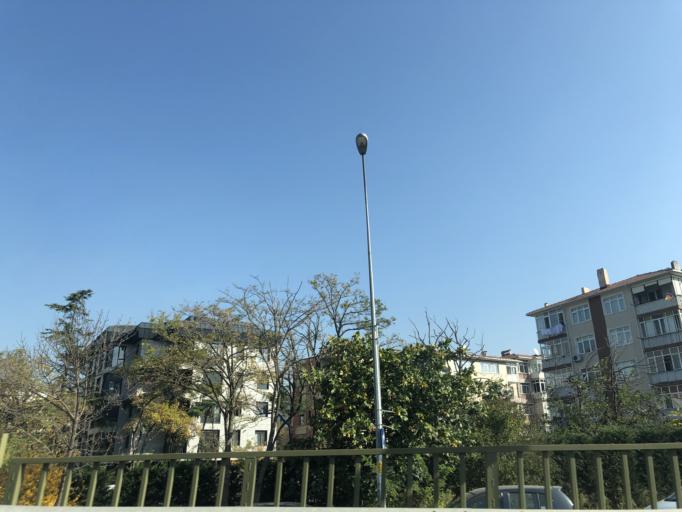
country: TR
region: Istanbul
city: UEskuedar
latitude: 40.9968
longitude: 29.0314
